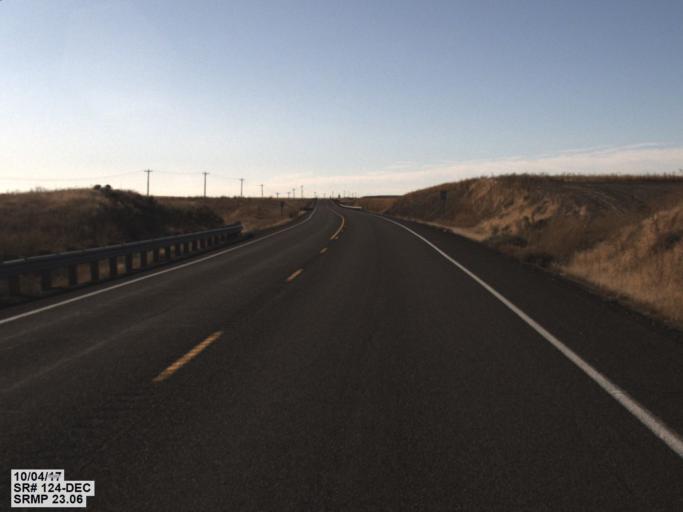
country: US
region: Washington
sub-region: Walla Walla County
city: Garrett
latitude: 46.2967
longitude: -118.5743
